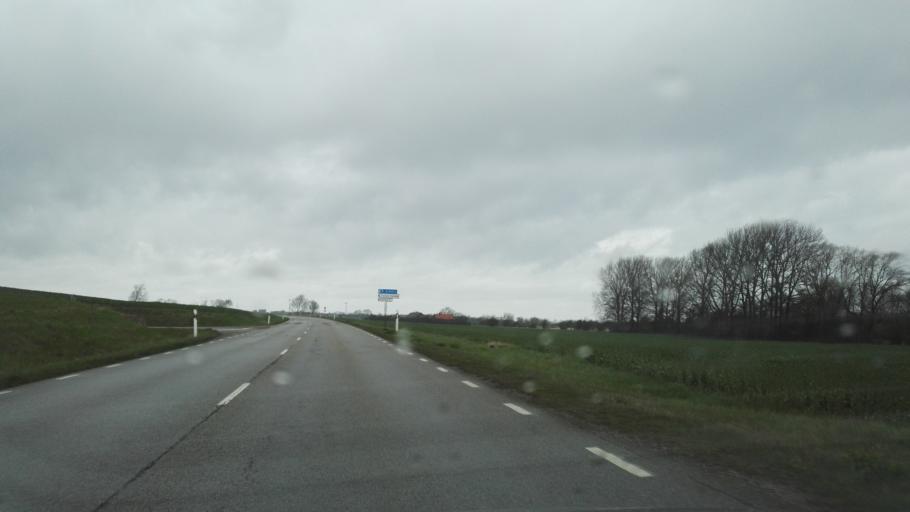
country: SE
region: Skane
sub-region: Simrishamns Kommun
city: Simrishamn
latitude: 55.5199
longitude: 14.3386
